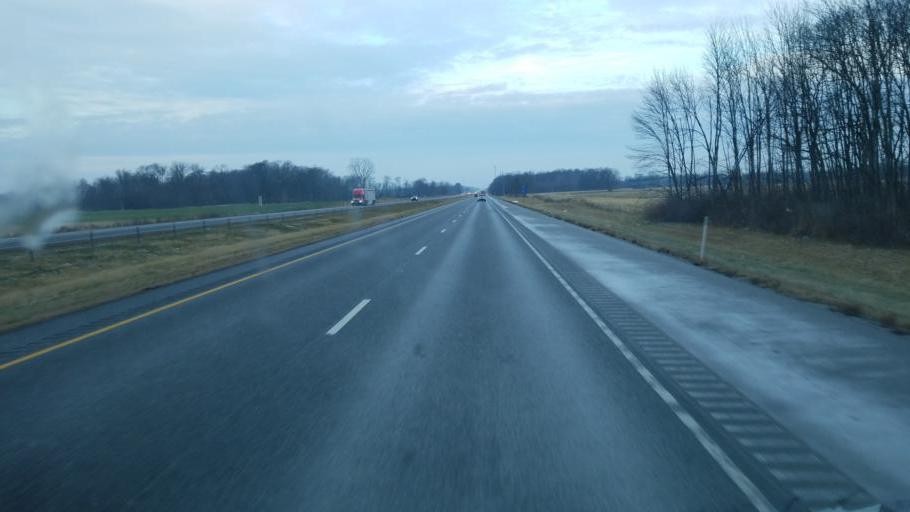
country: US
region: Indiana
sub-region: Hancock County
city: Greenfield
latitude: 39.8207
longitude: -85.8039
